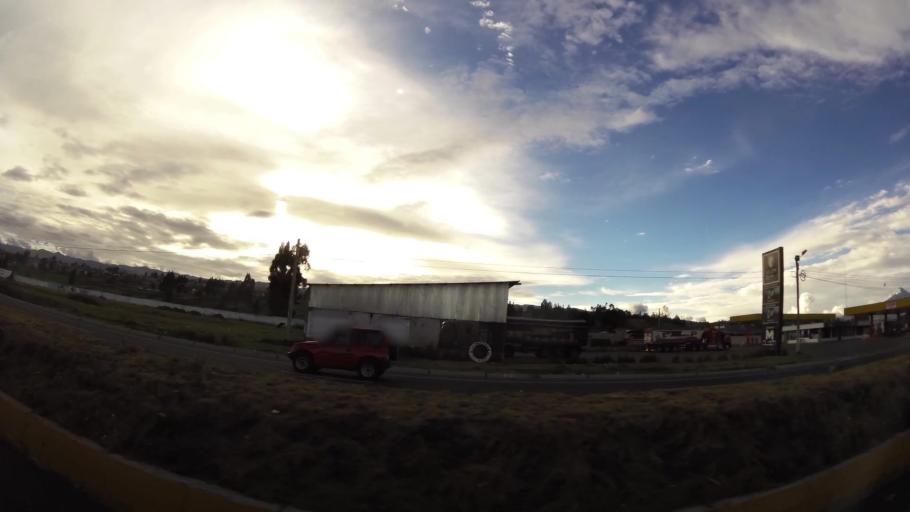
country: EC
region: Cotopaxi
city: Latacunga
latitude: -0.8969
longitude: -78.6290
